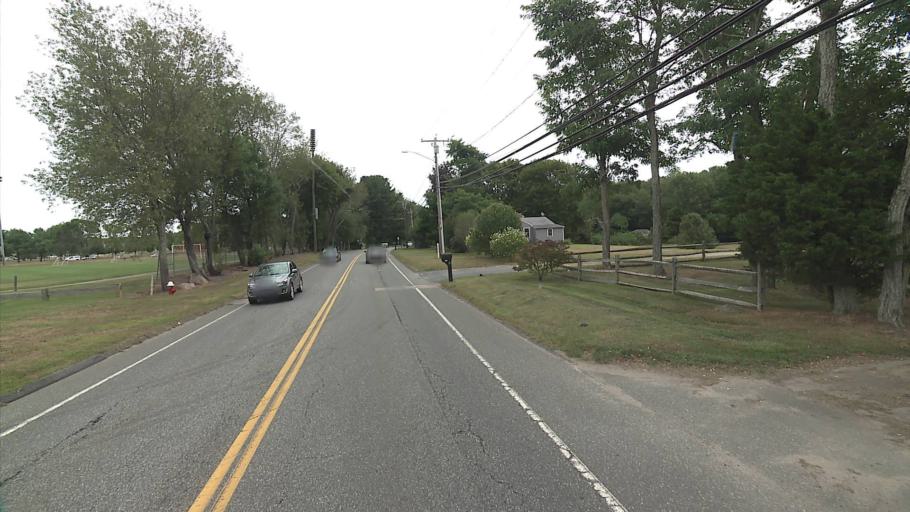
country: US
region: Connecticut
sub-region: New London County
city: Niantic
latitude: 41.3183
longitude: -72.2378
